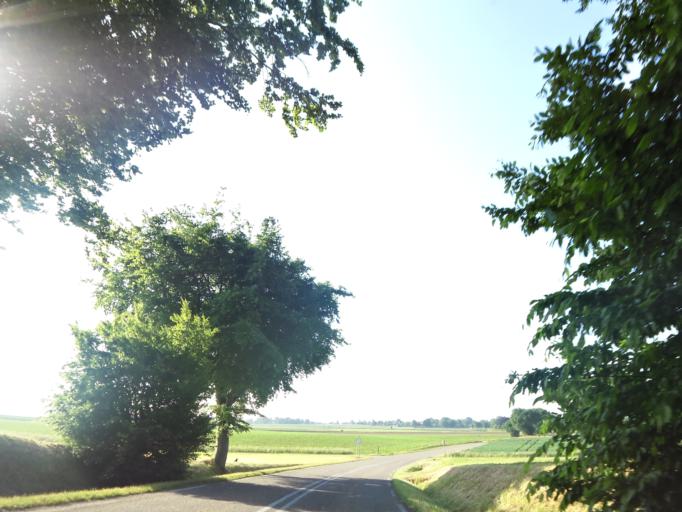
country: NL
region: Limburg
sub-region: Gemeente Beek
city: Beek
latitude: 50.9174
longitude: 5.8099
